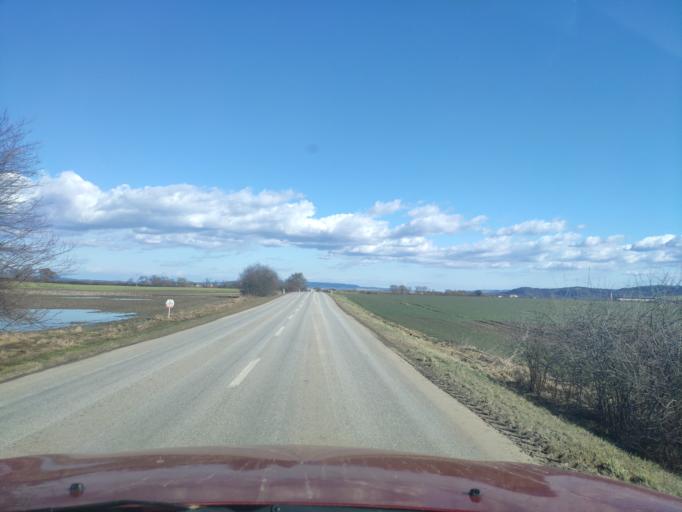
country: HU
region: Borsod-Abauj-Zemplen
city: Ozd
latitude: 48.2990
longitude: 20.2021
